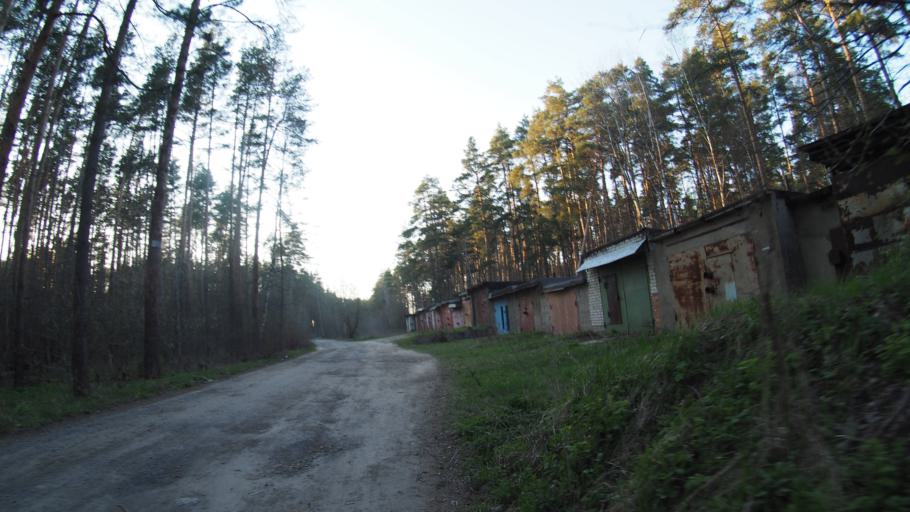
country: RU
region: Moskovskaya
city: Malyshevo
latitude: 55.5130
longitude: 38.3319
